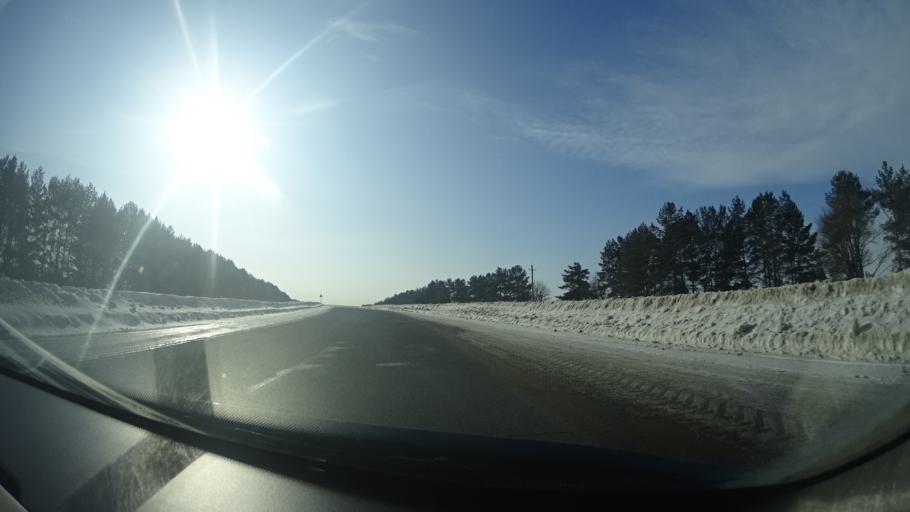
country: RU
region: Perm
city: Kuyeda
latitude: 56.4704
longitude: 55.5883
